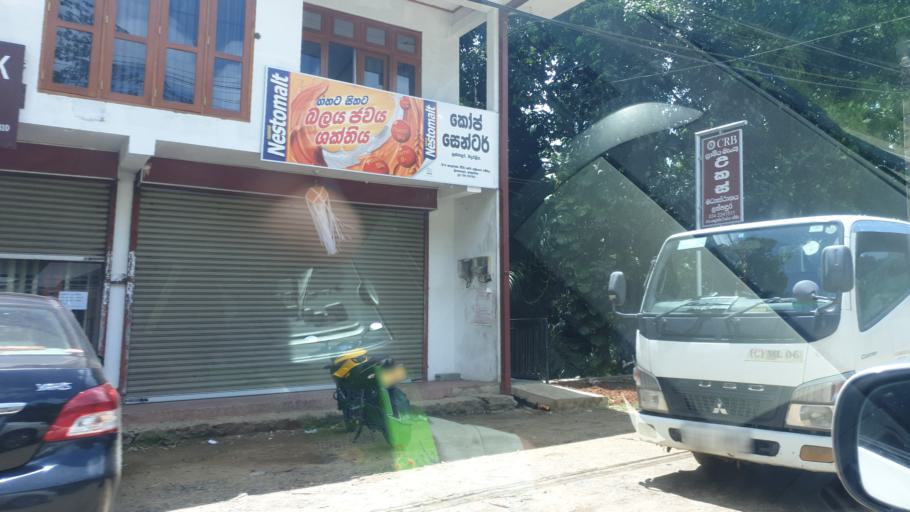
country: LK
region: Western
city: Horawala Junction
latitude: 6.5248
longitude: 80.2118
